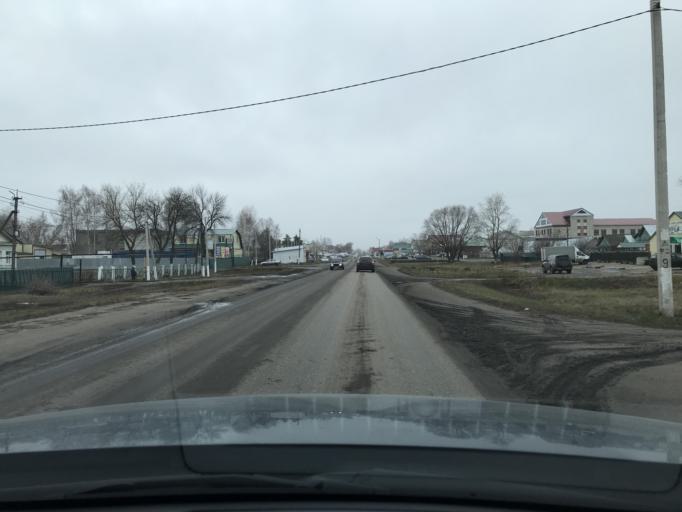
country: RU
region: Penza
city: Zemetchino
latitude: 53.4981
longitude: 42.6254
